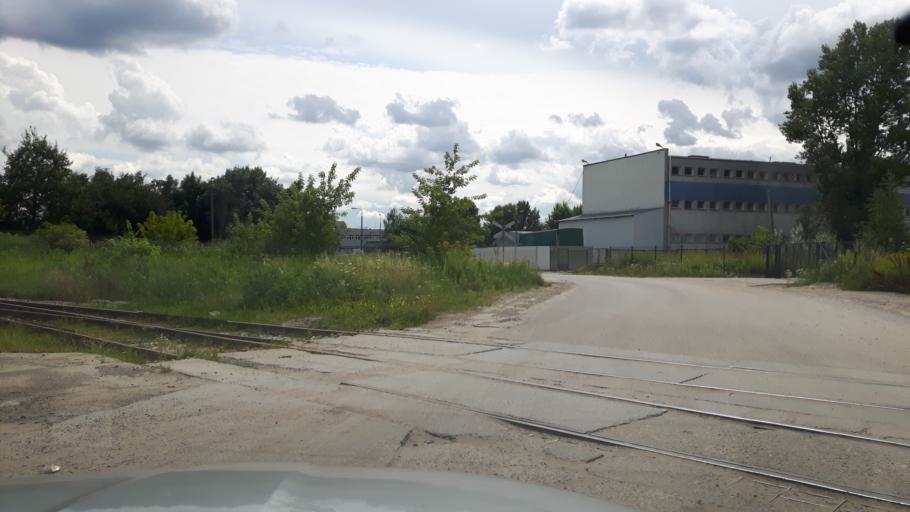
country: PL
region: Masovian Voivodeship
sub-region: Powiat wolominski
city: Zabki
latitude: 52.2720
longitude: 21.1238
